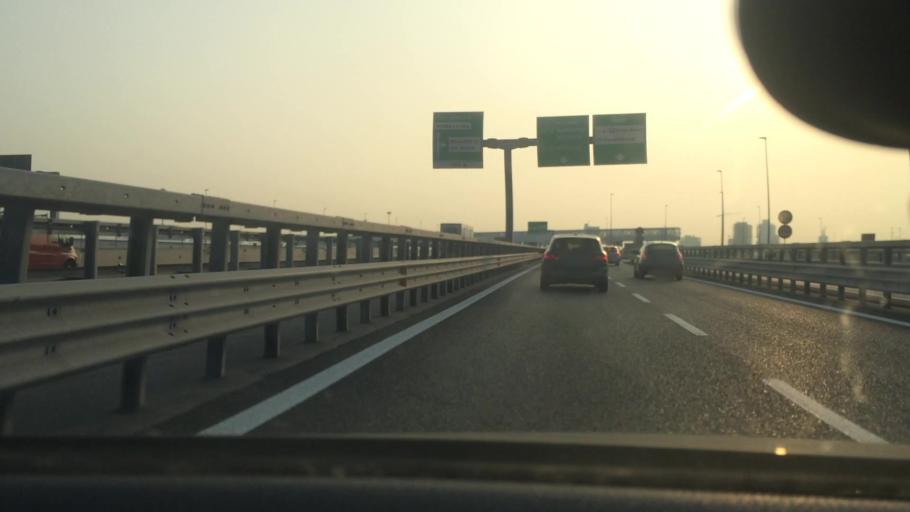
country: IT
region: Lombardy
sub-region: Citta metropolitana di Milano
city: Pero
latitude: 45.5129
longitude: 9.0965
